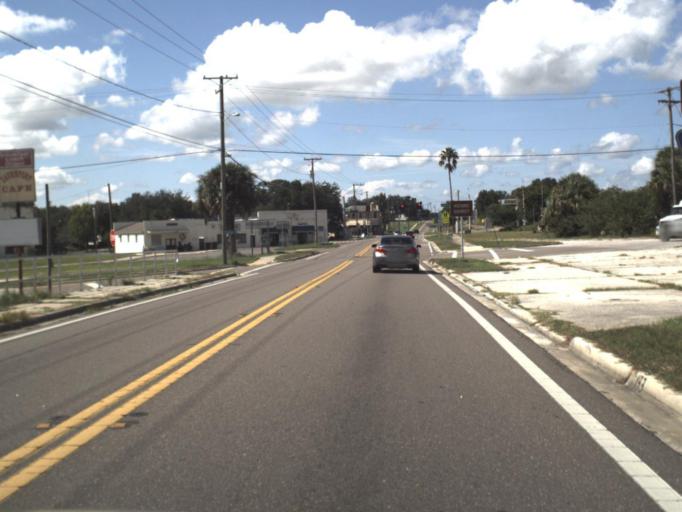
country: US
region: Florida
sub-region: Polk County
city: Davenport
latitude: 28.1610
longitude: -81.6021
